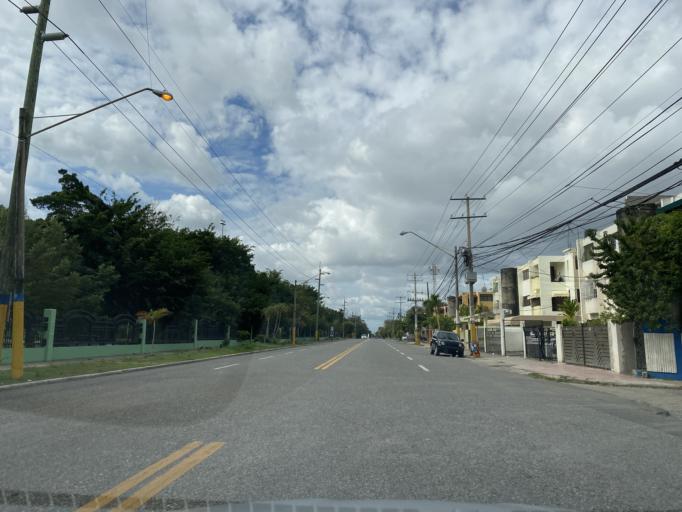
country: DO
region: Santo Domingo
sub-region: Santo Domingo
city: Santo Domingo Este
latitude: 18.4815
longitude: -69.8513
